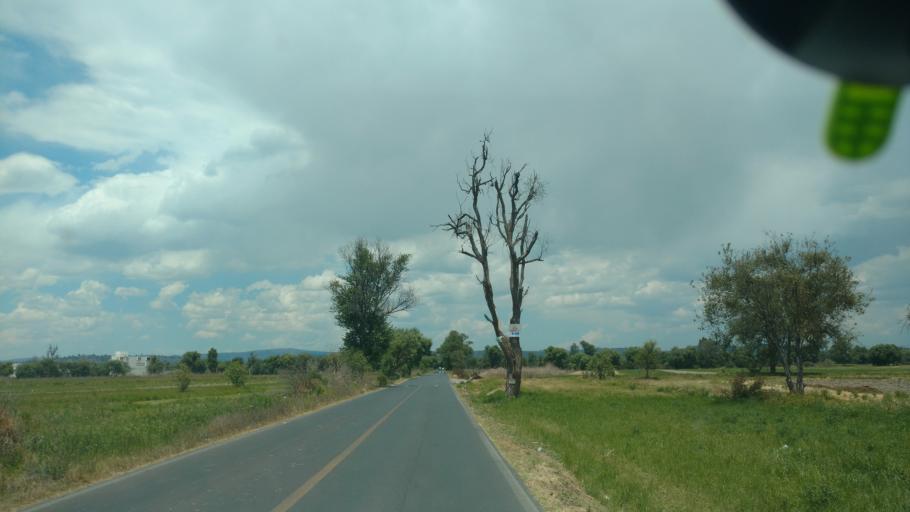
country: MX
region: Tlaxcala
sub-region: Tetlatlahuca
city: Tetlatlahuca
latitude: 19.1964
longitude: -98.2860
